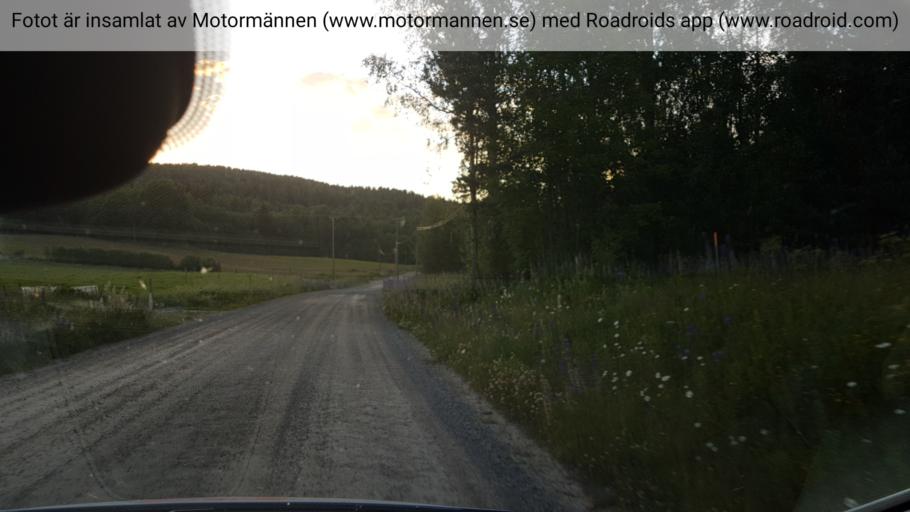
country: SE
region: Vaermland
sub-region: Sunne Kommun
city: Sunne
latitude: 59.6848
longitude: 12.8940
